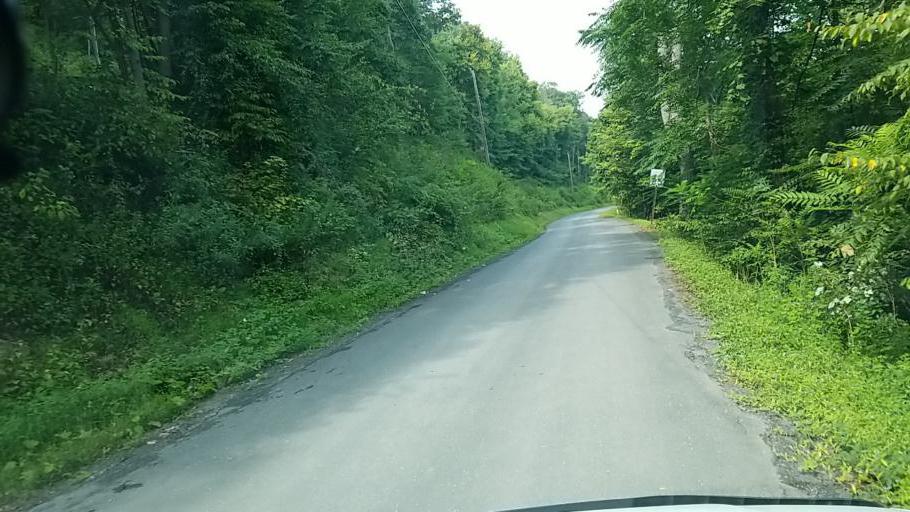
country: US
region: Pennsylvania
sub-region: Dauphin County
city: Millersburg
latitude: 40.5263
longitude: -76.9483
